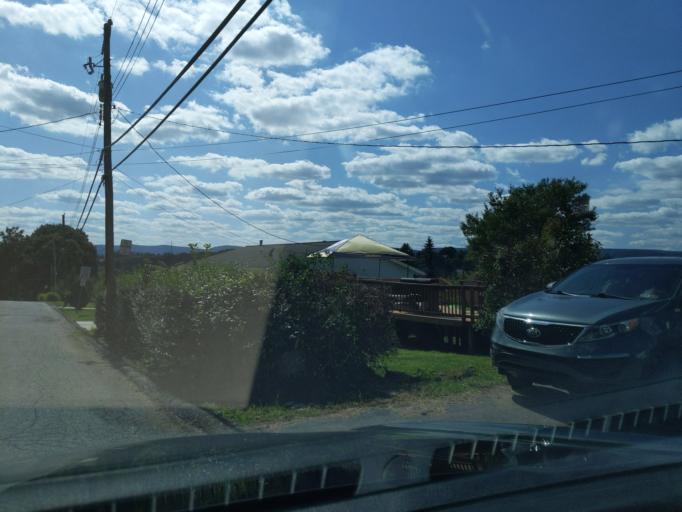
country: US
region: Pennsylvania
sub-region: Blair County
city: Altoona
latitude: 40.5174
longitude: -78.3719
